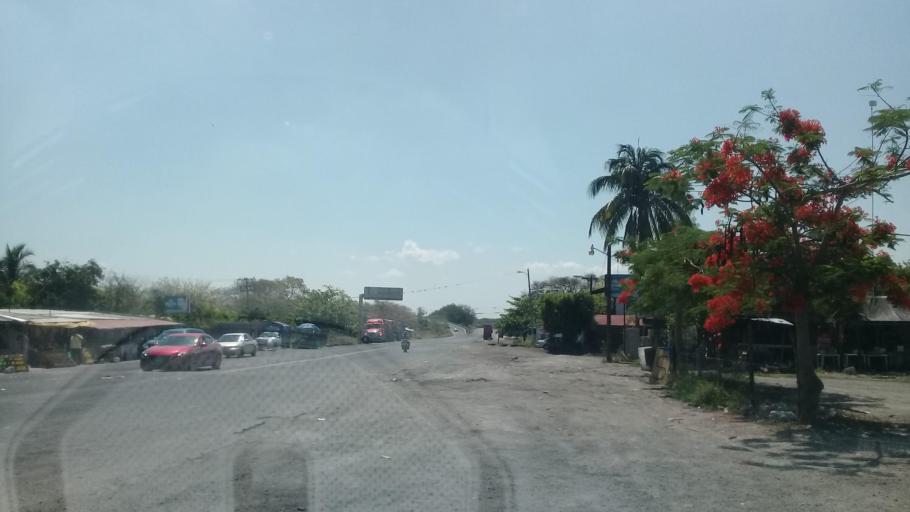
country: MX
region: Veracruz
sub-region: Emiliano Zapata
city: Plan del Rio
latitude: 19.3932
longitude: -96.6192
